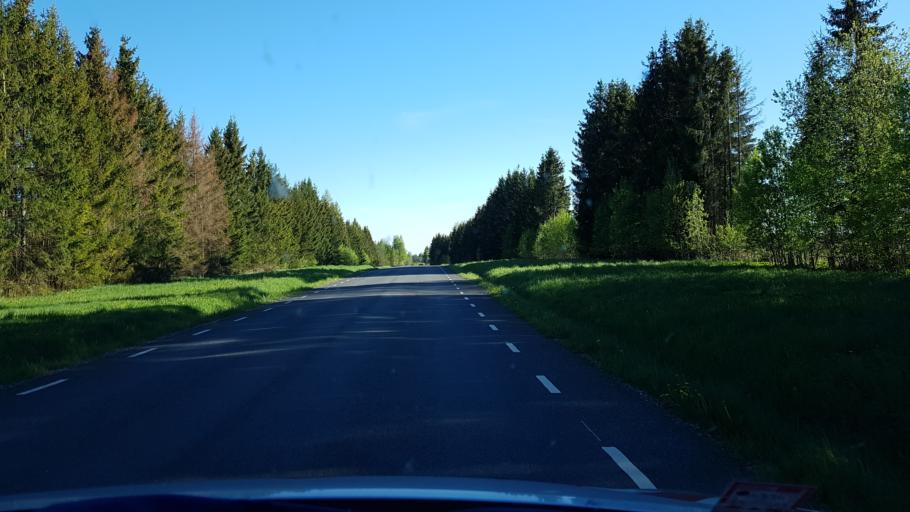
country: EE
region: Vorumaa
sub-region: Voru linn
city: Voru
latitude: 57.9474
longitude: 26.9551
